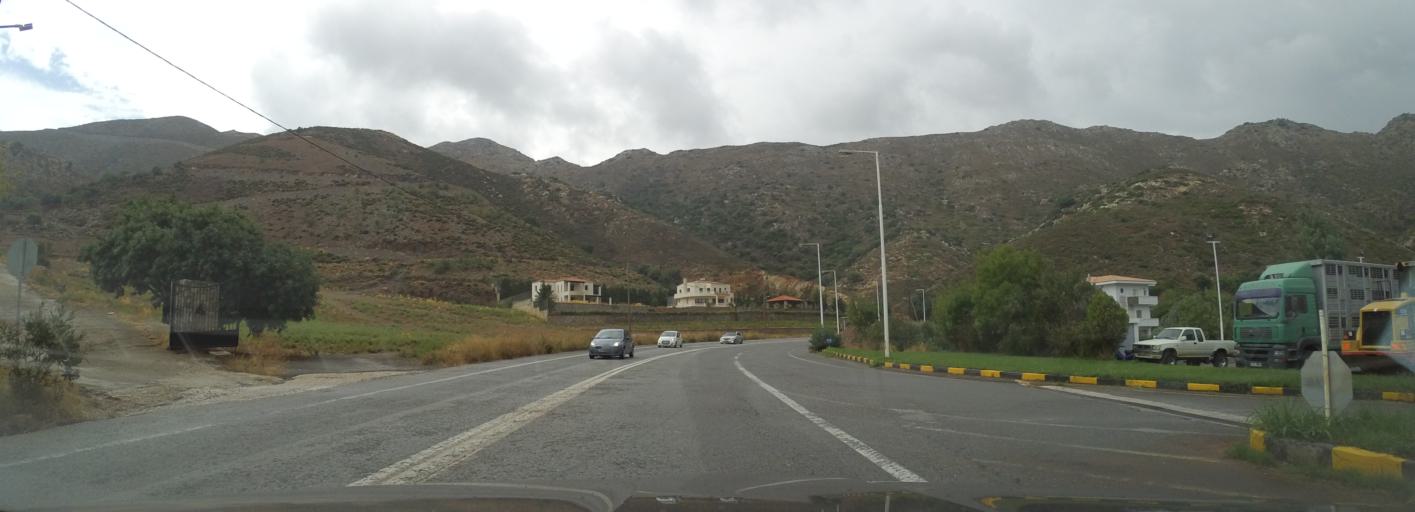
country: GR
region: Crete
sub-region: Nomos Rethymnis
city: Anogeia
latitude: 35.3832
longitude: 24.9186
